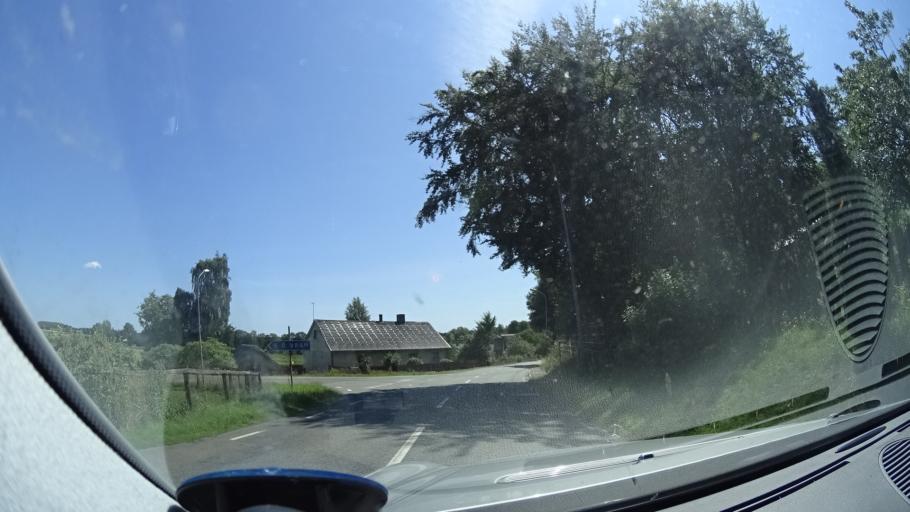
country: SE
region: Skane
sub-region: Kristianstads Kommun
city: Degeberga
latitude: 55.8886
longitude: 14.0135
